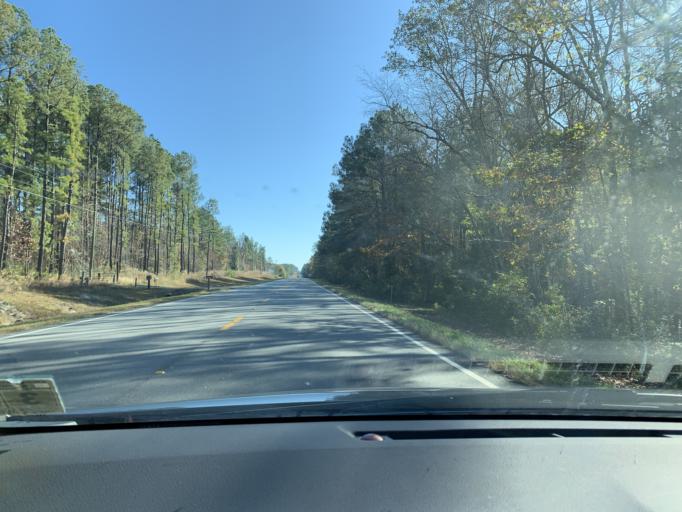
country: US
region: Georgia
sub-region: Ben Hill County
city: Fitzgerald
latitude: 31.7750
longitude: -83.0609
